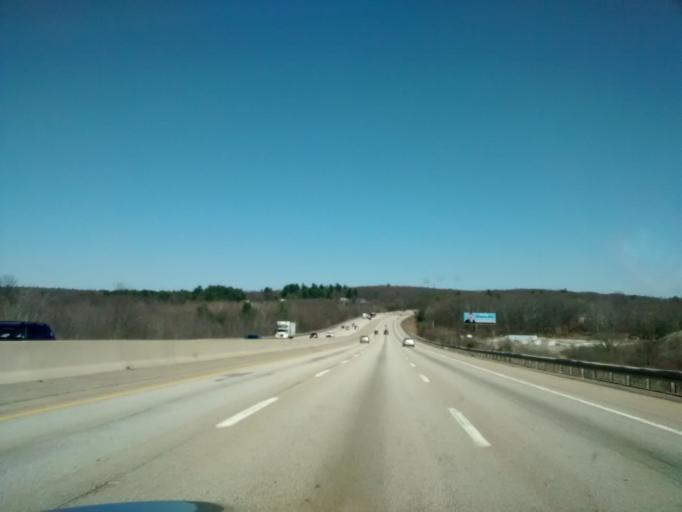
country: US
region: Massachusetts
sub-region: Worcester County
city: Grafton
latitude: 42.2253
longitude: -71.7047
